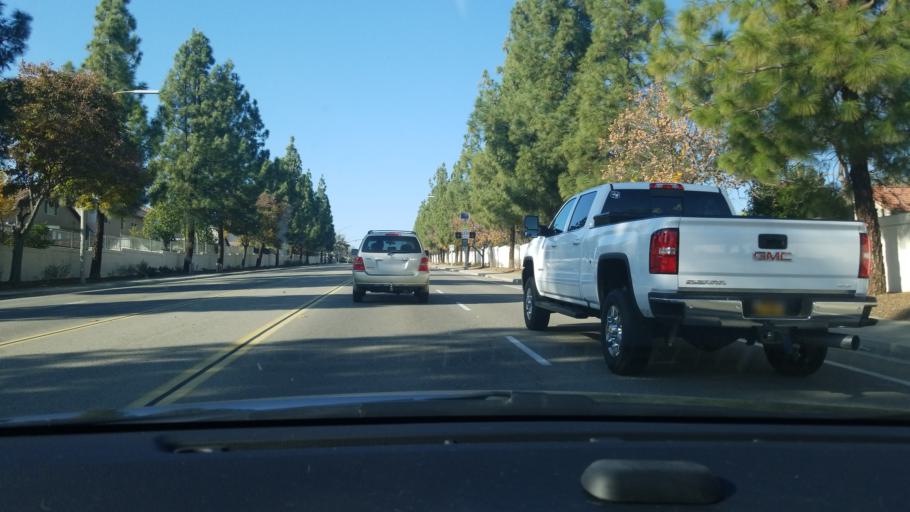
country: US
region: California
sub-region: Riverside County
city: Murrieta
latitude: 33.5784
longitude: -117.2115
